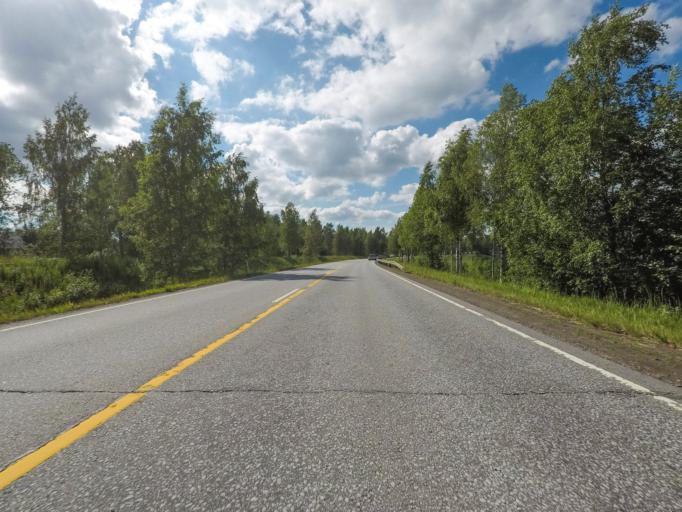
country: FI
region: Southern Savonia
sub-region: Savonlinna
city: Kerimaeki
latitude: 61.8060
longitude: 29.2824
